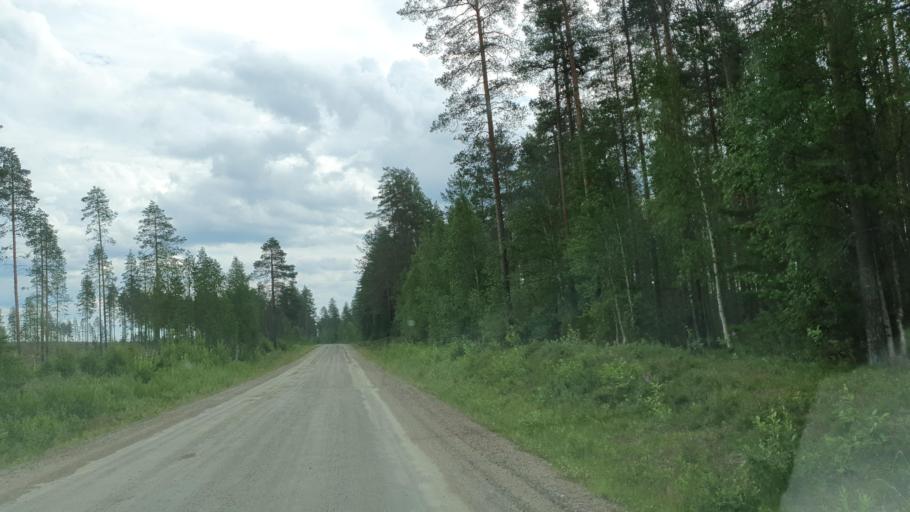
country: FI
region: Kainuu
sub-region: Kehys-Kainuu
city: Kuhmo
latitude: 64.7235
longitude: 29.6783
